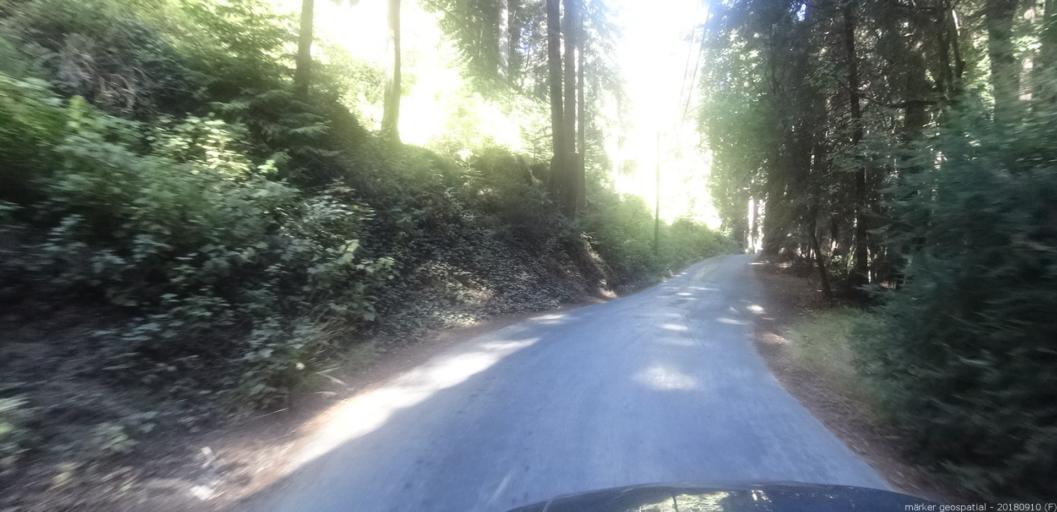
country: US
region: California
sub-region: Monterey County
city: Carmel Valley Village
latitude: 36.3981
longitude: -121.8853
